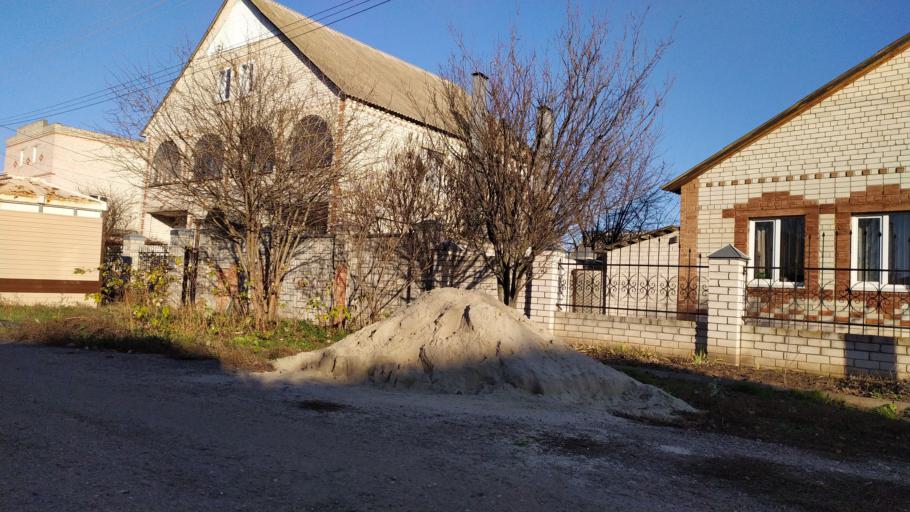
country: RU
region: Kursk
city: Kursk
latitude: 51.6451
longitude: 36.1378
